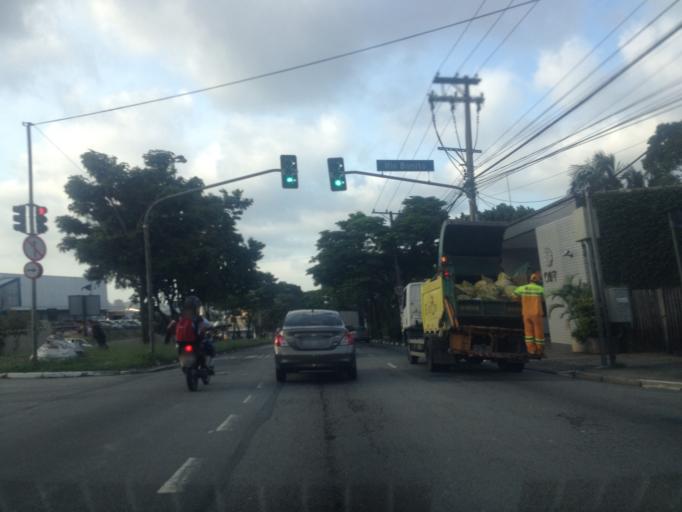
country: BR
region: Sao Paulo
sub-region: Diadema
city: Diadema
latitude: -23.6758
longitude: -46.7123
